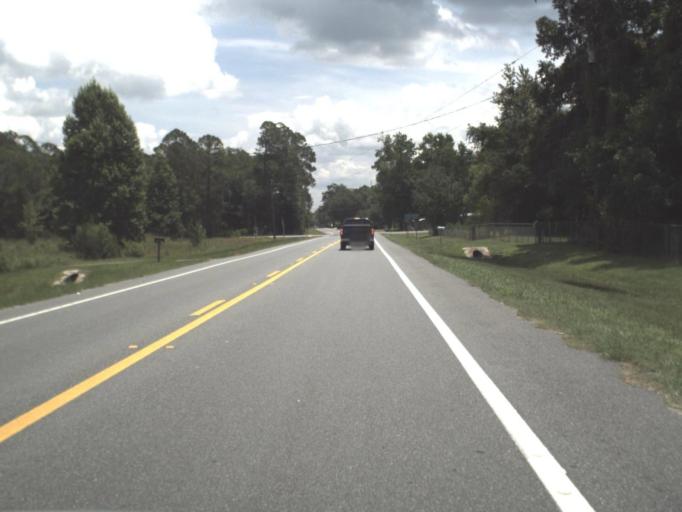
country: US
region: Florida
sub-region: Union County
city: Lake Butler
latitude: 30.0209
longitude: -82.3554
